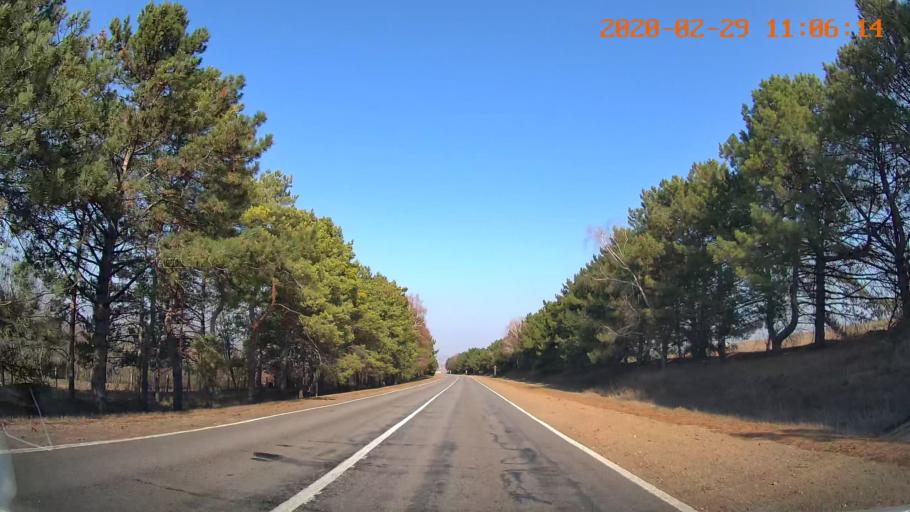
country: MD
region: Criuleni
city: Criuleni
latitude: 47.2122
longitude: 29.1890
